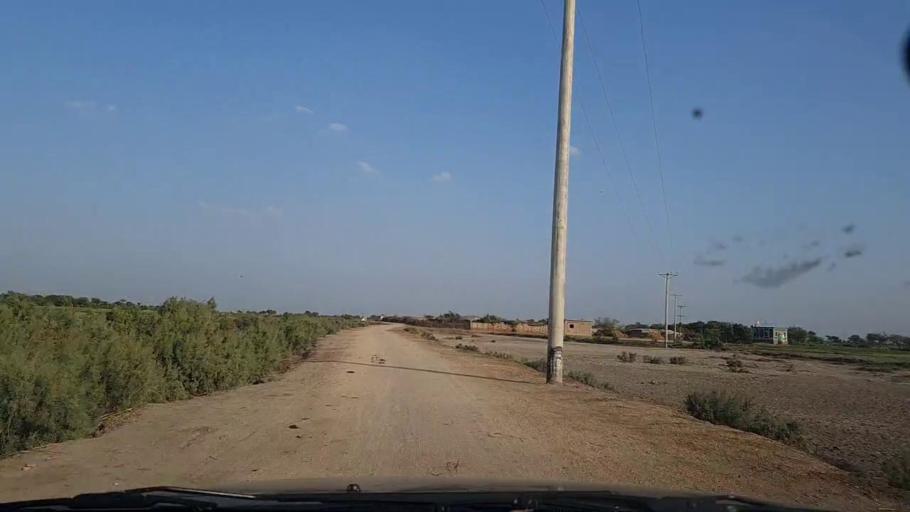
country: PK
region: Sindh
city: Daro Mehar
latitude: 24.7484
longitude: 68.0917
